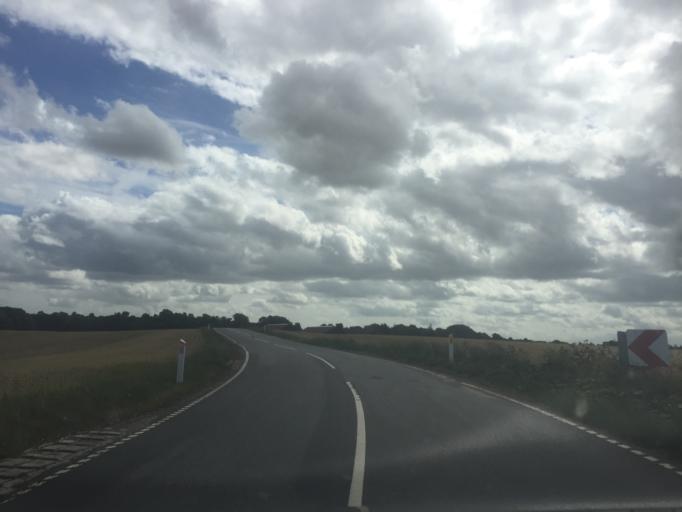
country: DK
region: Capital Region
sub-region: Hoje-Taastrup Kommune
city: Flong
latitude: 55.6955
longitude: 12.2345
